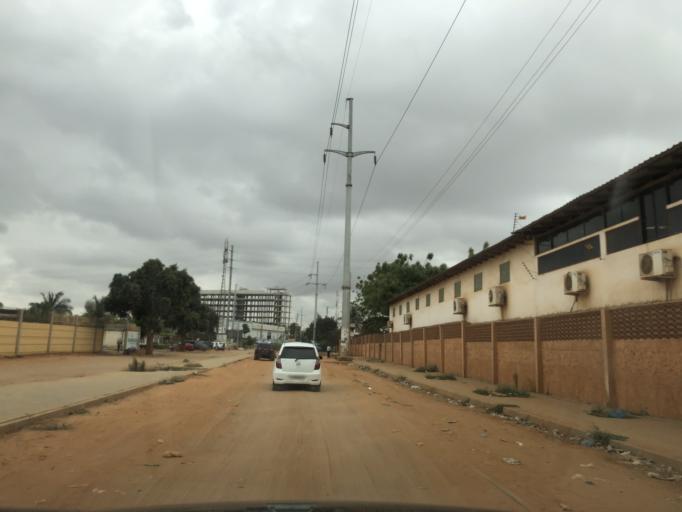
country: AO
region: Luanda
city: Luanda
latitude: -8.9008
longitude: 13.1978
